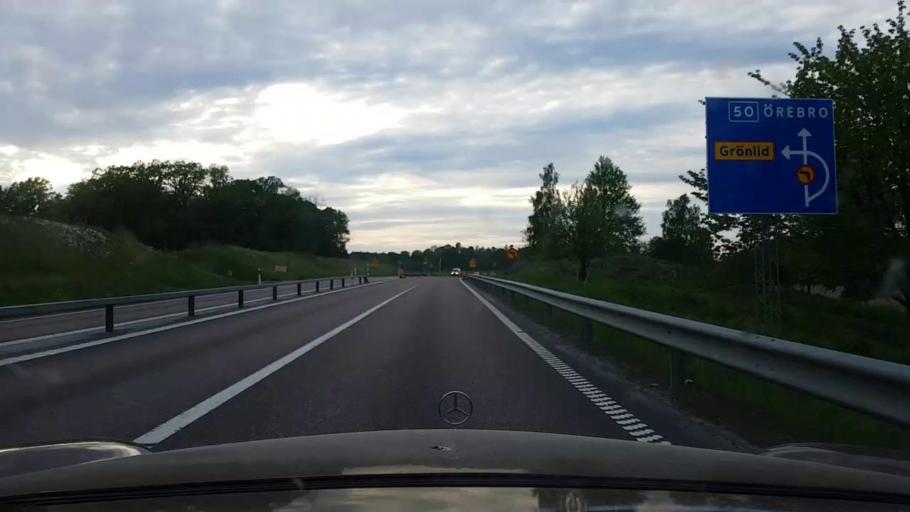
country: SE
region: OErebro
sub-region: Askersunds Kommun
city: Askersund
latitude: 58.8536
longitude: 14.9099
